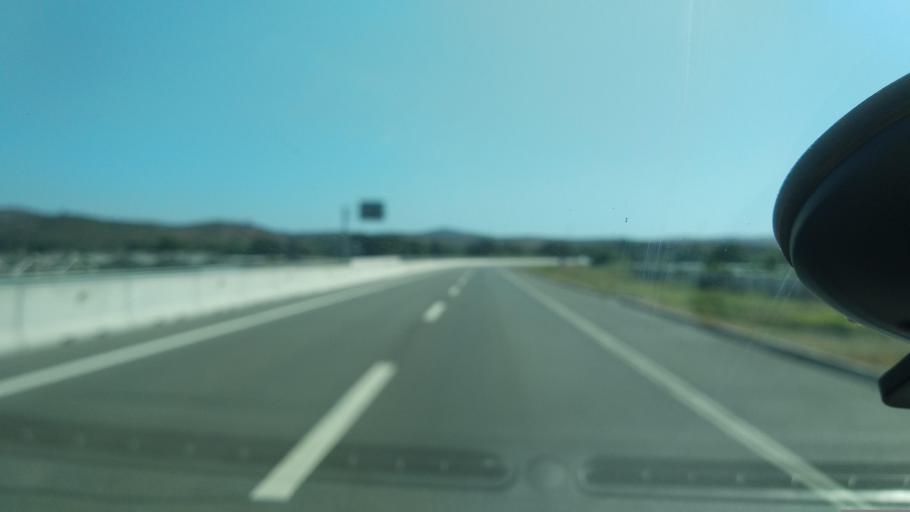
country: CL
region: Valparaiso
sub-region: Provincia de Marga Marga
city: Limache
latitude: -32.9792
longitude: -71.3068
